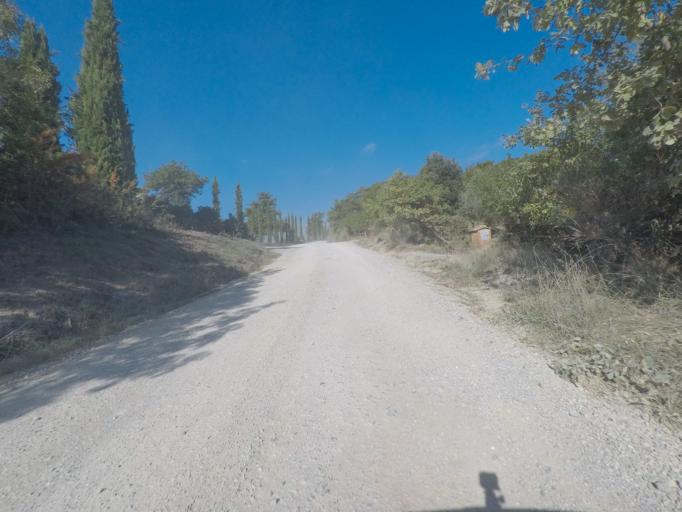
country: IT
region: Tuscany
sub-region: Provincia di Siena
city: Castellina in Chianti
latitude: 43.4357
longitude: 11.3305
